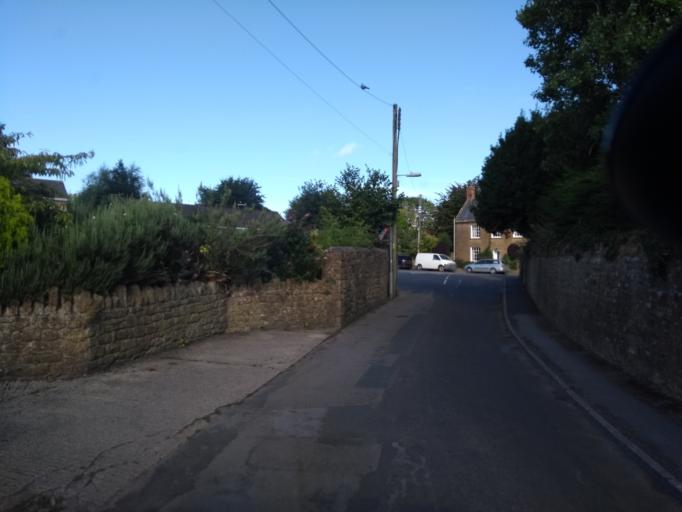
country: GB
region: England
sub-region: Somerset
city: South Petherton
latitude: 50.9489
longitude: -2.8121
